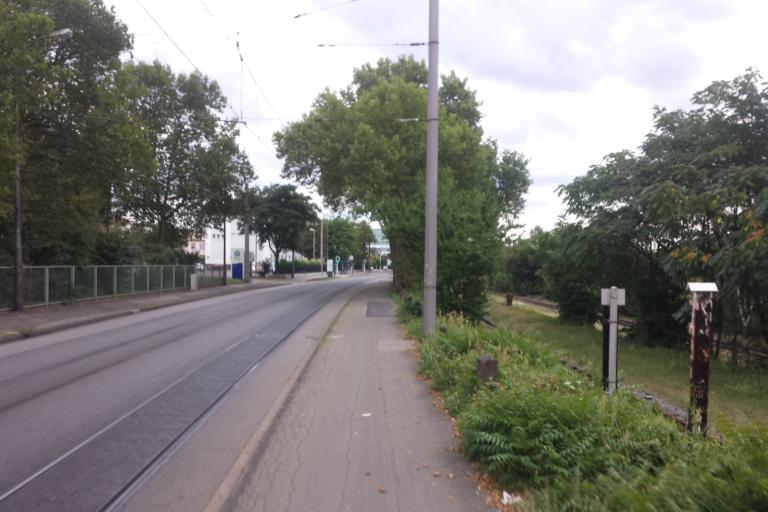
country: DE
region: Baden-Wuerttemberg
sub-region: Karlsruhe Region
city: Mannheim
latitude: 49.5321
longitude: 8.4635
